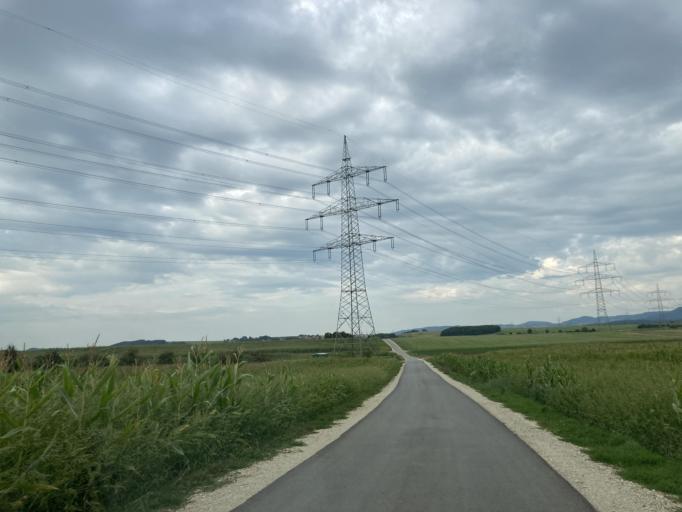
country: DE
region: Baden-Wuerttemberg
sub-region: Freiburg Region
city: Hufingen
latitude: 47.9199
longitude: 8.5441
